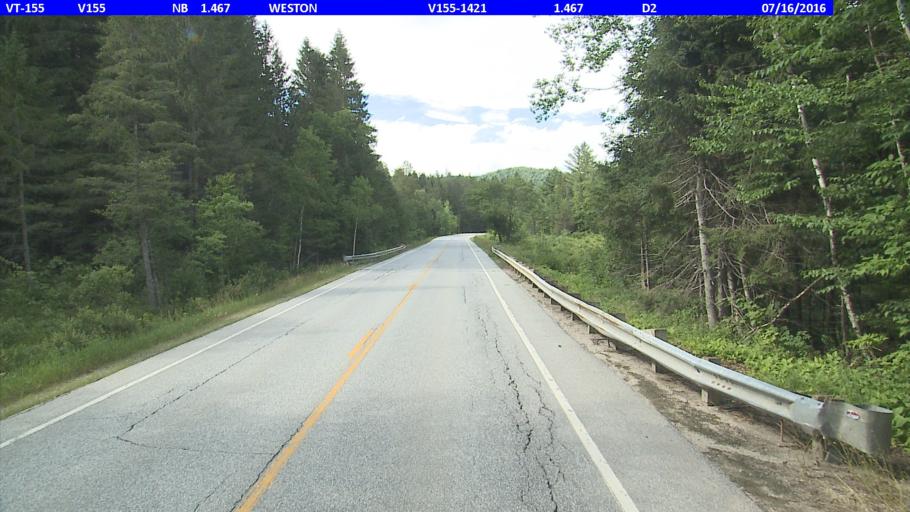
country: US
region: Vermont
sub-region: Windsor County
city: Chester
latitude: 43.3566
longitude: -72.7950
